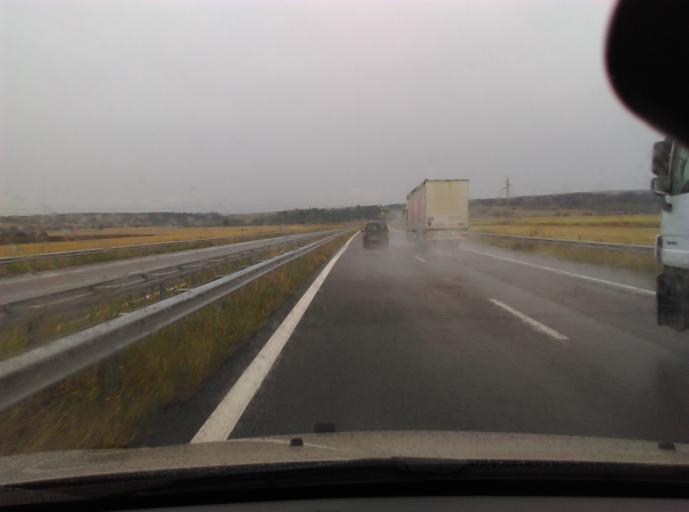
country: BG
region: Khaskovo
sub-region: Obshtina Dimitrovgrad
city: Dimitrovgrad
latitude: 42.0379
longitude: 25.5354
